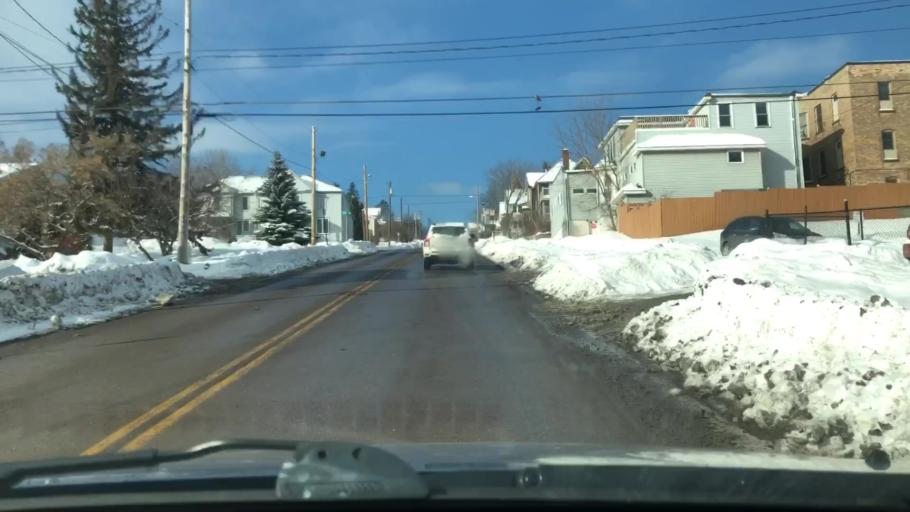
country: US
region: Minnesota
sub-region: Saint Louis County
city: Duluth
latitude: 46.7898
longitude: -92.1028
